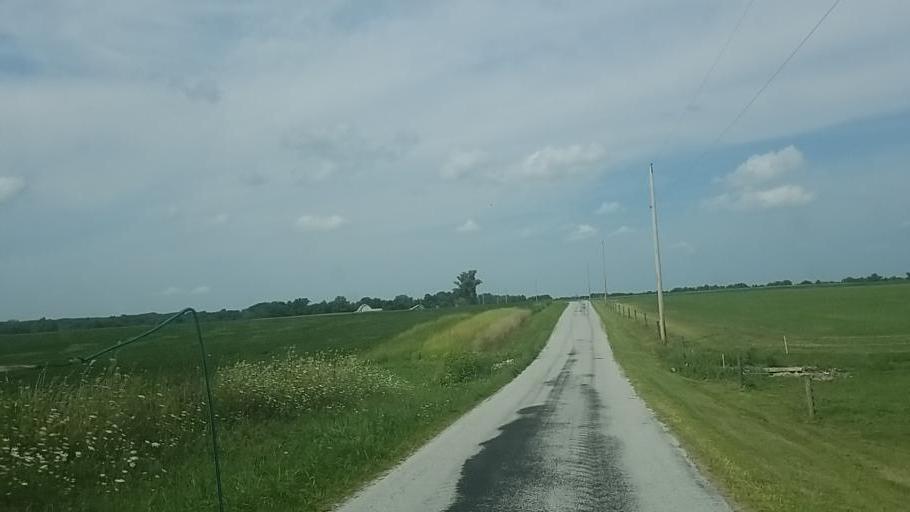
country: US
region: Ohio
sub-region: Hardin County
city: Forest
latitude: 40.7841
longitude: -83.5618
